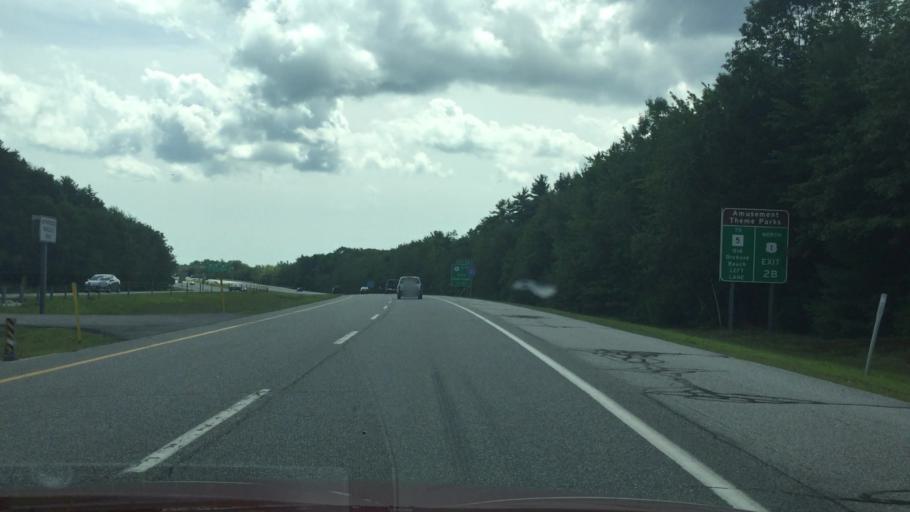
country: US
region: Maine
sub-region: York County
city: Saco
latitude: 43.5167
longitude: -70.4411
